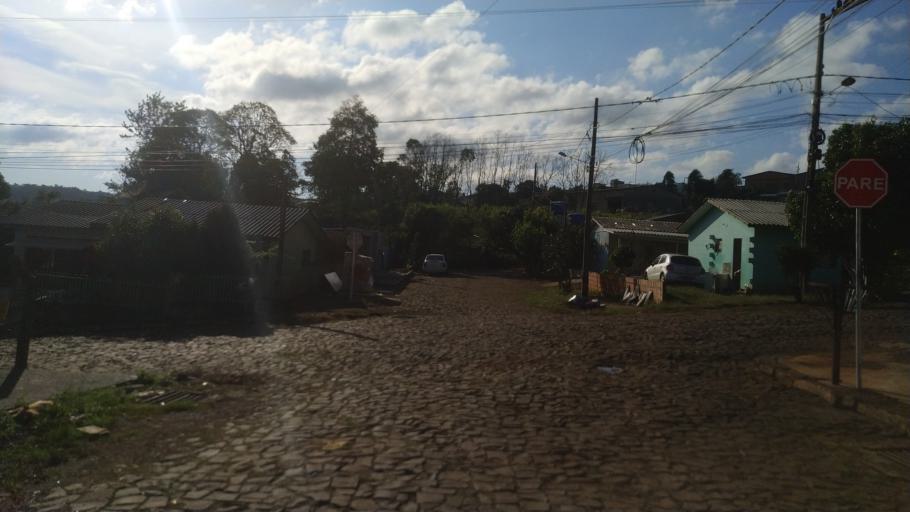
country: BR
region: Santa Catarina
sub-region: Chapeco
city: Chapeco
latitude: -27.0668
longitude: -52.6088
